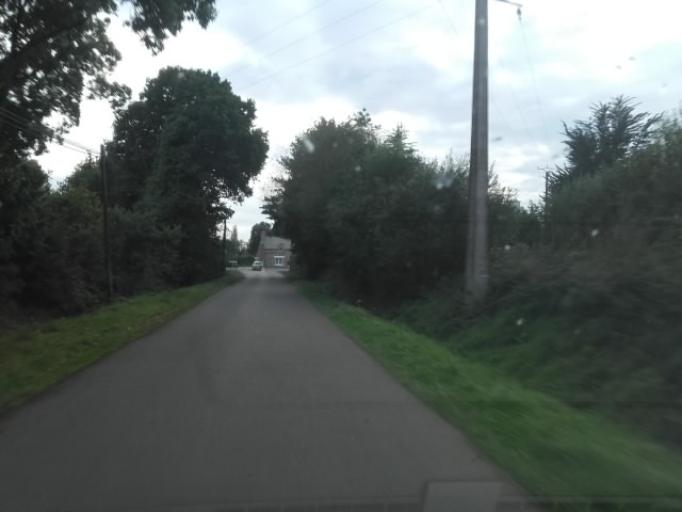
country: FR
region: Brittany
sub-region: Departement des Cotes-d'Armor
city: Lanvollon
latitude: 48.6216
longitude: -2.9739
